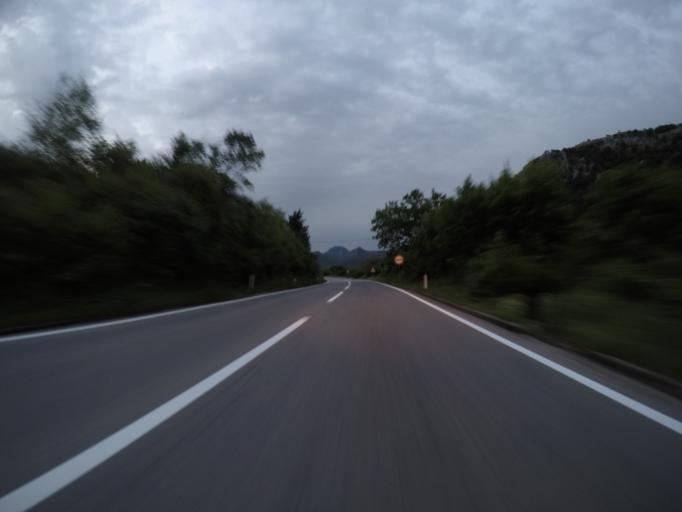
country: ME
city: Petrovac na Moru
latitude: 42.2027
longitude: 18.9595
